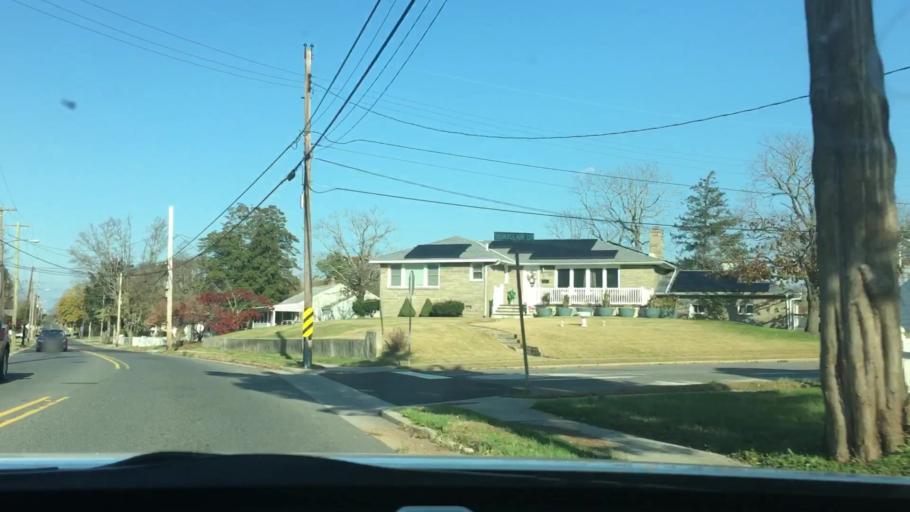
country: US
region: New Jersey
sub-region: Atlantic County
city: Absecon
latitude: 39.4107
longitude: -74.5056
